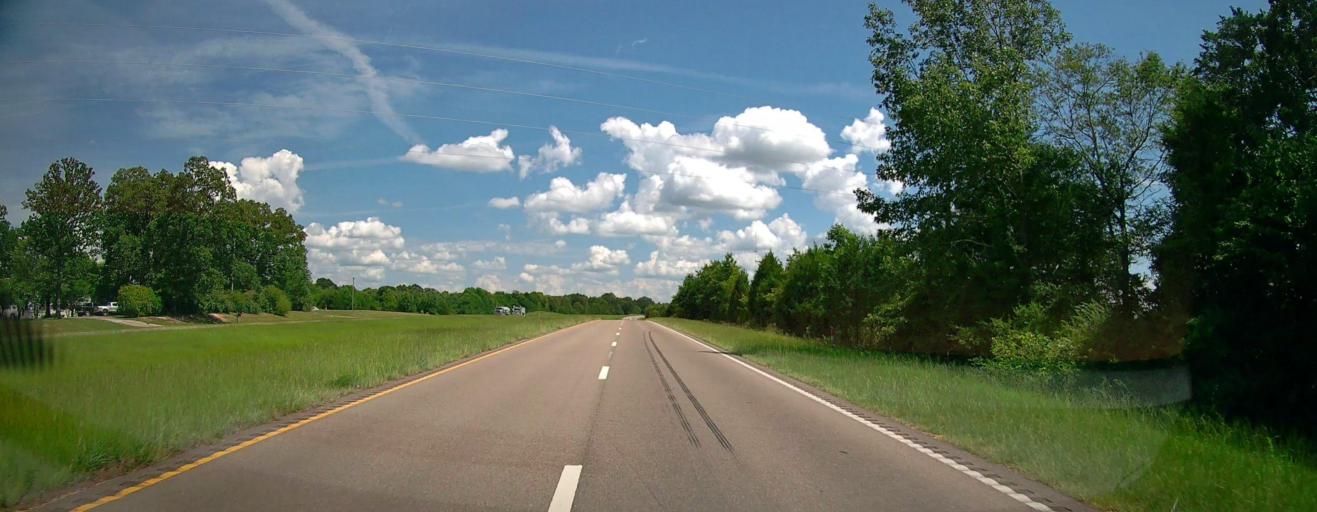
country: US
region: Mississippi
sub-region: Monroe County
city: Amory
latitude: 33.9578
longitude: -88.6093
